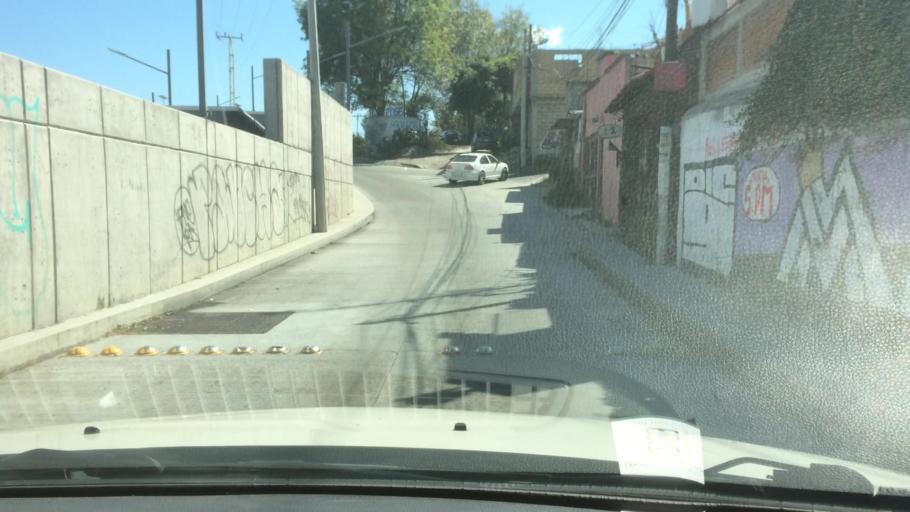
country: MX
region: Mexico City
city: Xochimilco
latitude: 19.2418
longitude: -99.1490
